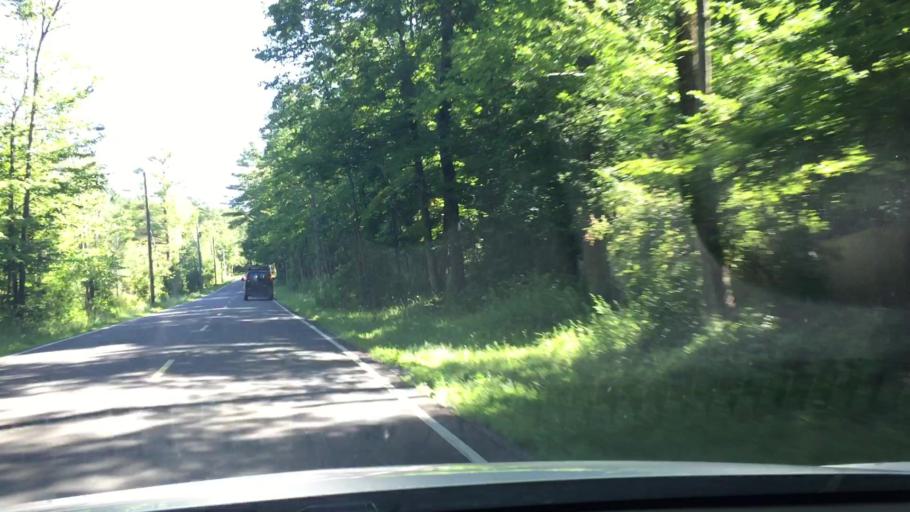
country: US
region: Massachusetts
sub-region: Berkshire County
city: Richmond
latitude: 42.3881
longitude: -73.3403
